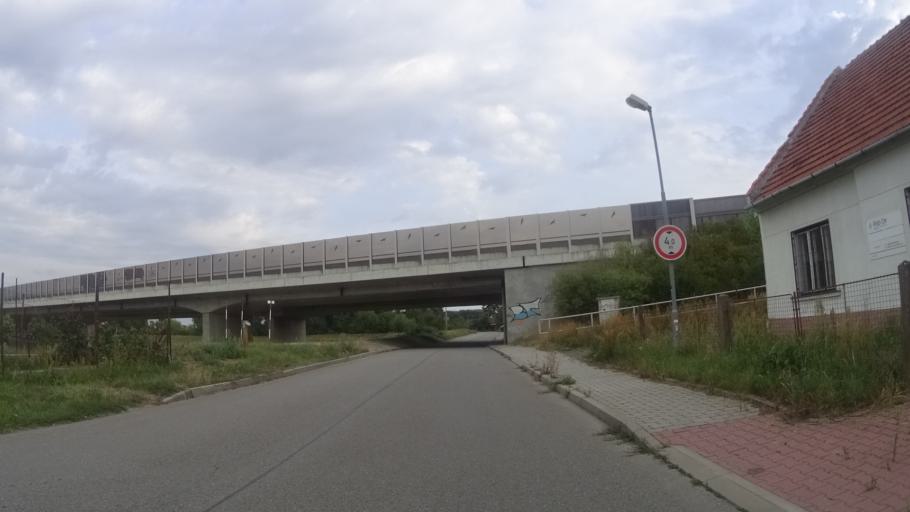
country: CZ
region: Zlin
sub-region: Okres Kromeriz
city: Kromeriz
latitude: 49.3124
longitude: 17.3913
